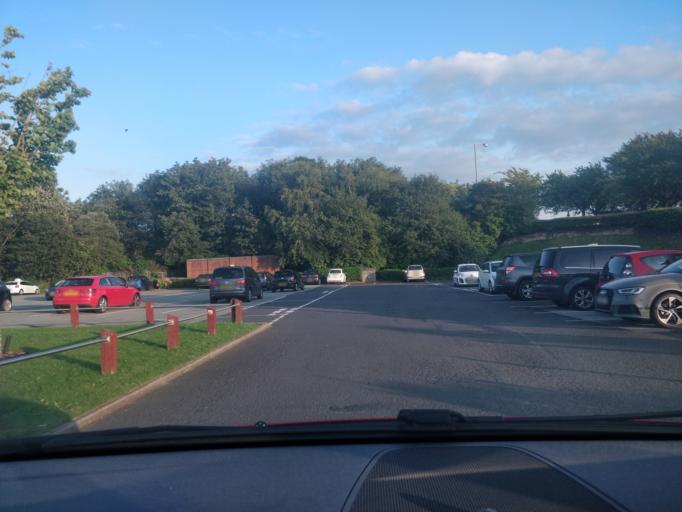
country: GB
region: England
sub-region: Lancashire
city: Preston
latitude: 53.7726
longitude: -2.6771
